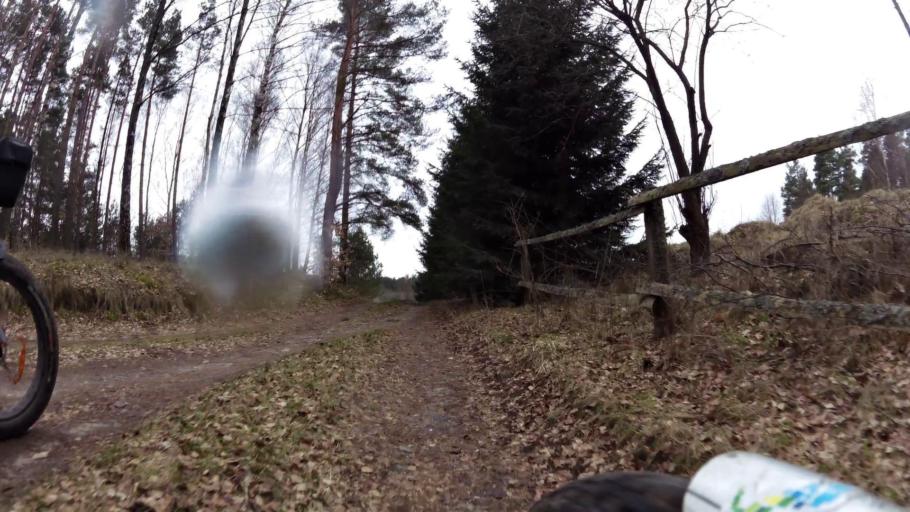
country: PL
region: Pomeranian Voivodeship
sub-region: Powiat bytowski
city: Trzebielino
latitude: 54.0829
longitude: 17.1181
